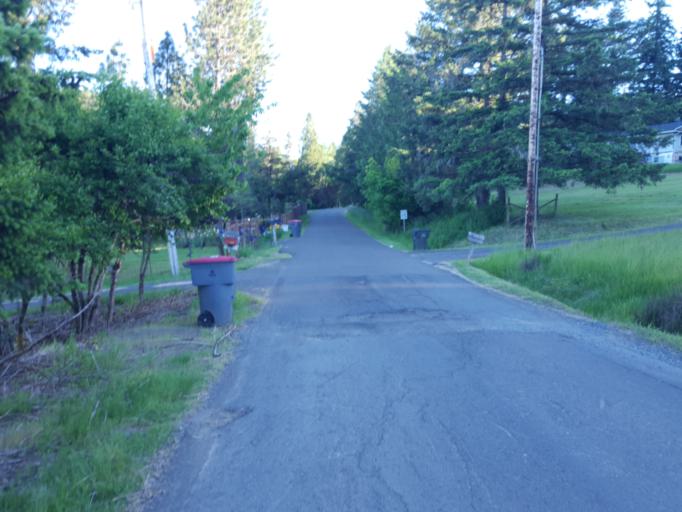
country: US
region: Oregon
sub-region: Yamhill County
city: McMinnville
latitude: 45.2233
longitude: -123.2690
